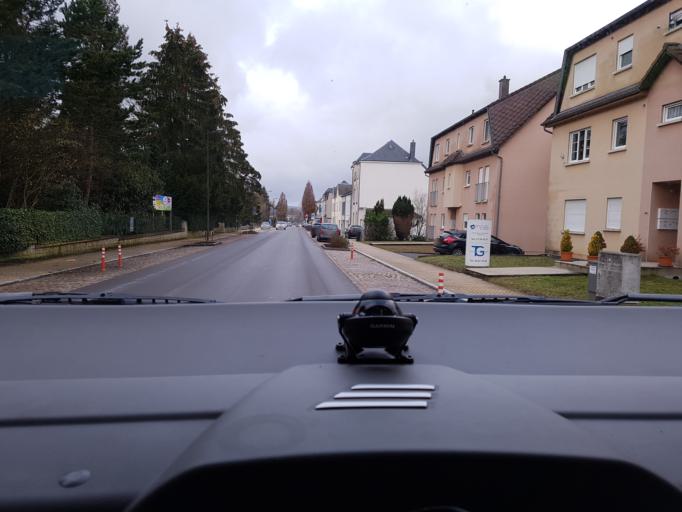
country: LU
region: Luxembourg
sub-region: Canton de Capellen
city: Steinfort
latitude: 49.6597
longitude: 5.9248
